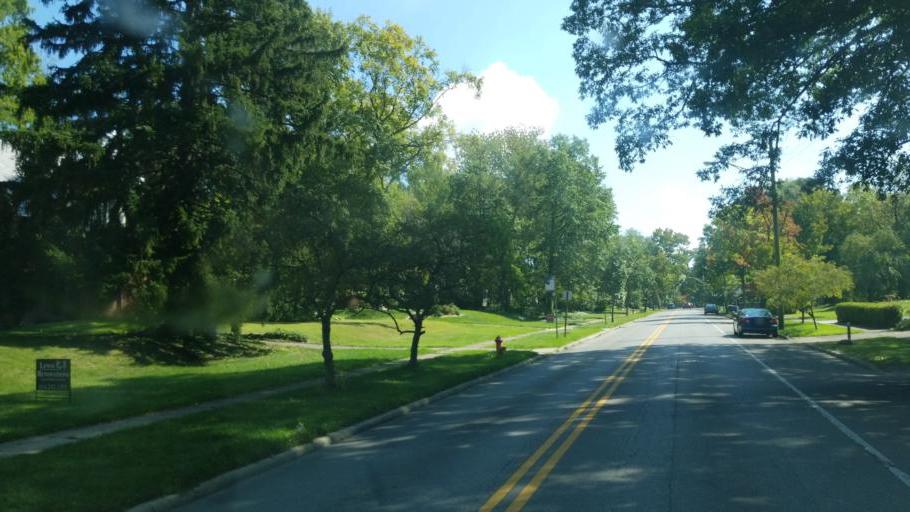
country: US
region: Ohio
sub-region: Franklin County
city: Grandview Heights
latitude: 40.0315
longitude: -83.0117
